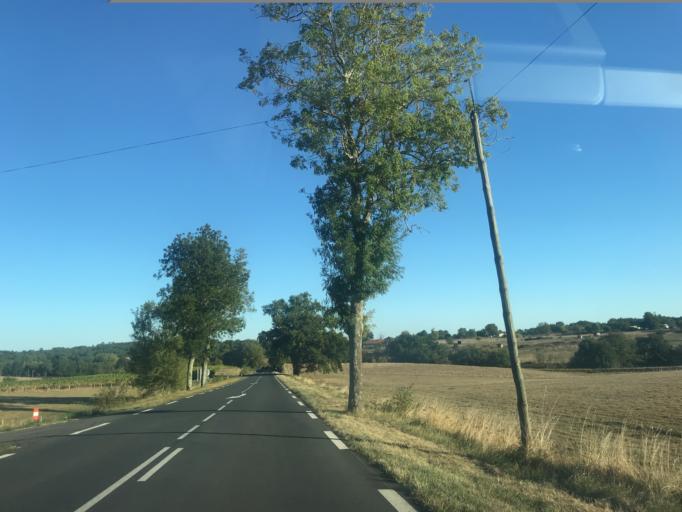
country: FR
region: Poitou-Charentes
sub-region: Departement de la Charente-Maritime
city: Montguyon
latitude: 45.1769
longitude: -0.1159
